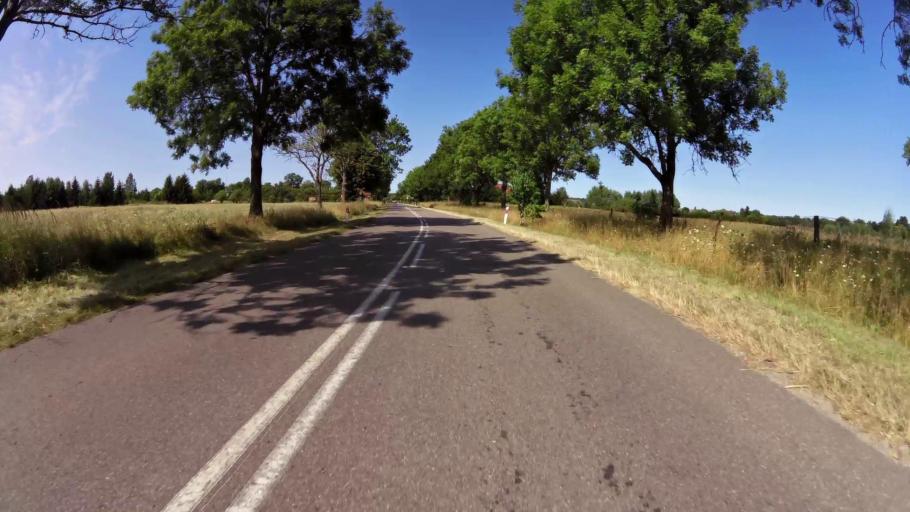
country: PL
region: West Pomeranian Voivodeship
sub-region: Powiat stargardzki
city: Suchan
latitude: 53.3034
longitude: 15.3694
